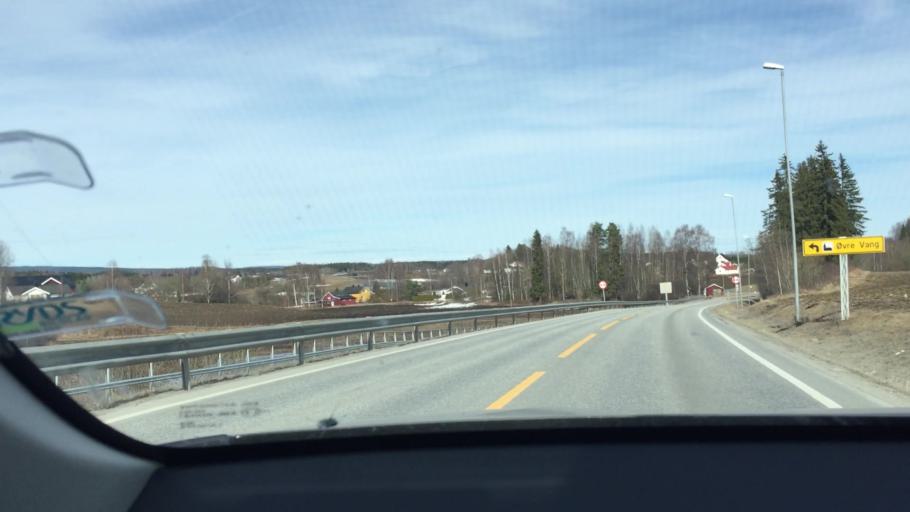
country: NO
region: Hedmark
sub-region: Stange
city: Stange
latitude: 60.8184
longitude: 11.1875
